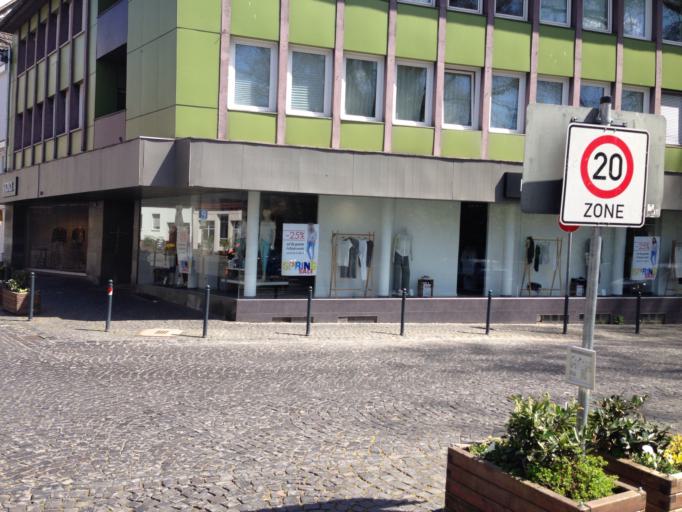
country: DE
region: Hesse
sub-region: Regierungsbezirk Giessen
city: Lich
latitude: 50.5191
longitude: 8.8191
